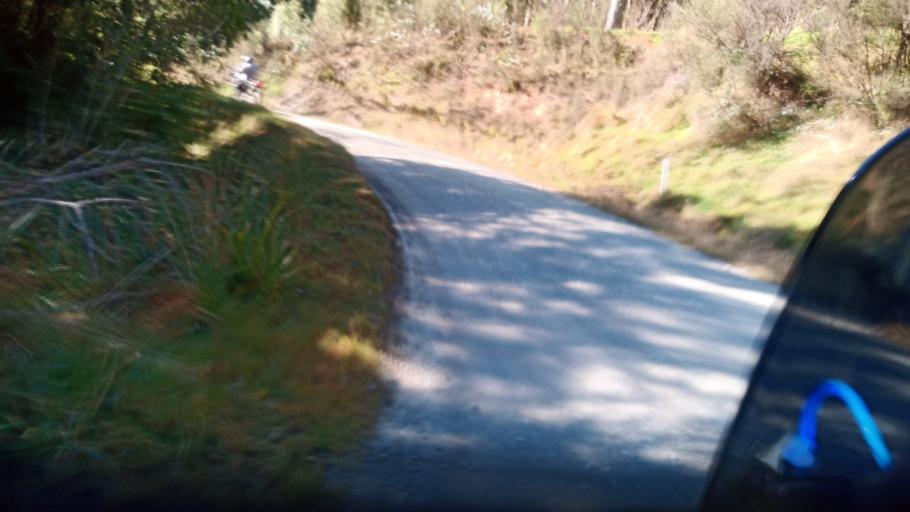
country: NZ
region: Hawke's Bay
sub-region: Wairoa District
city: Wairoa
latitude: -38.6612
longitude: 177.4882
